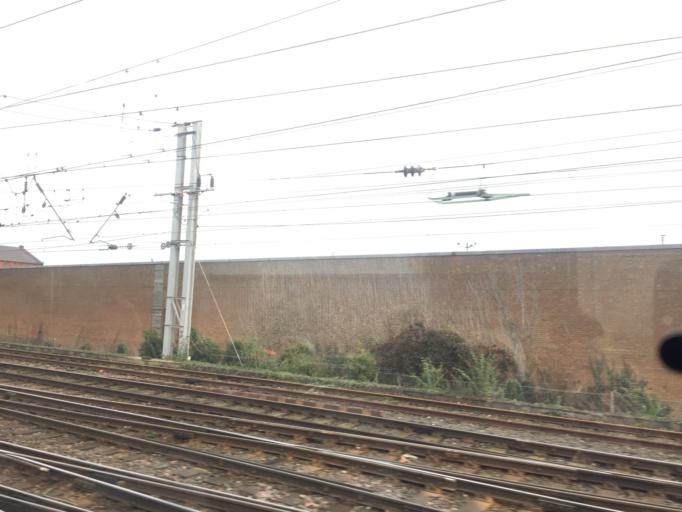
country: GB
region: England
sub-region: Cumbria
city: Carlisle
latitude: 54.8879
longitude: -2.9298
